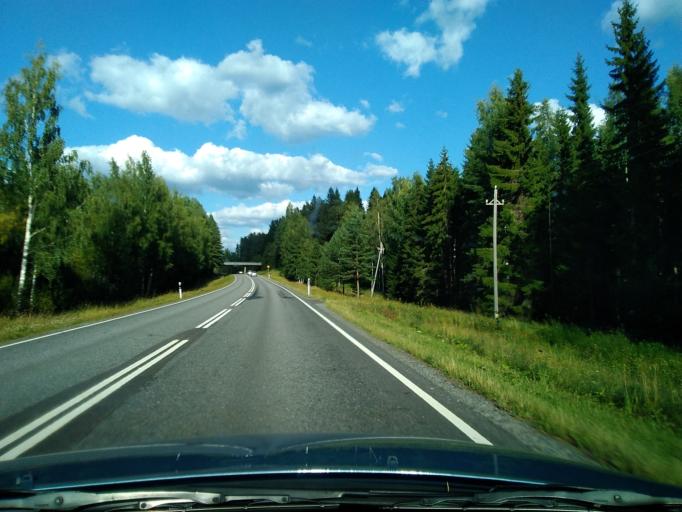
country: FI
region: Pirkanmaa
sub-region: Ylae-Pirkanmaa
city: Maenttae
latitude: 62.0072
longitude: 24.6623
